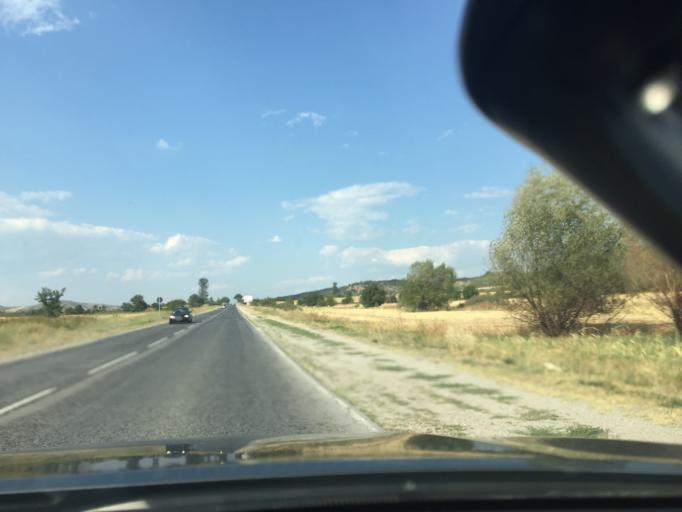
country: BG
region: Kyustendil
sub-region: Obshtina Boboshevo
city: Boboshevo
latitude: 42.1821
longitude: 23.0541
